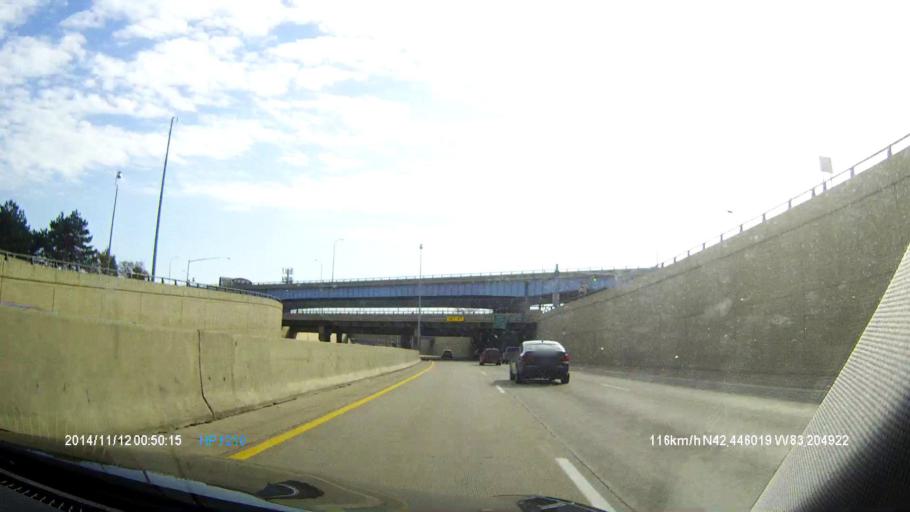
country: US
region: Michigan
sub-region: Oakland County
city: Oak Park
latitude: 42.4457
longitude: -83.2046
